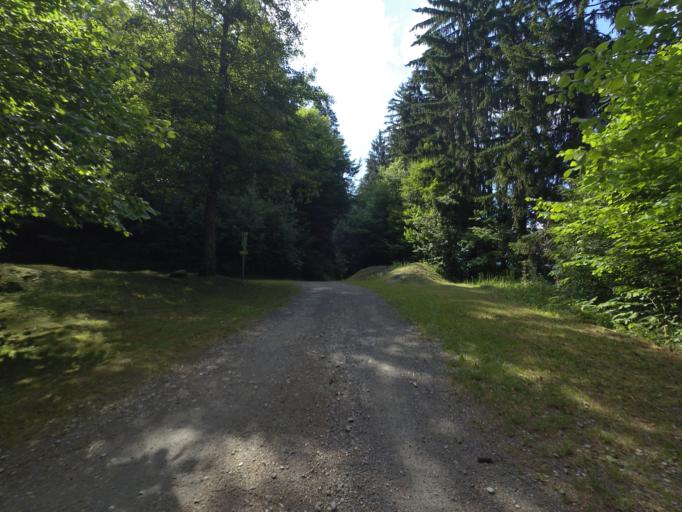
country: AT
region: Carinthia
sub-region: Politischer Bezirk Villach Land
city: Ferndorf
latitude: 46.7649
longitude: 13.6241
